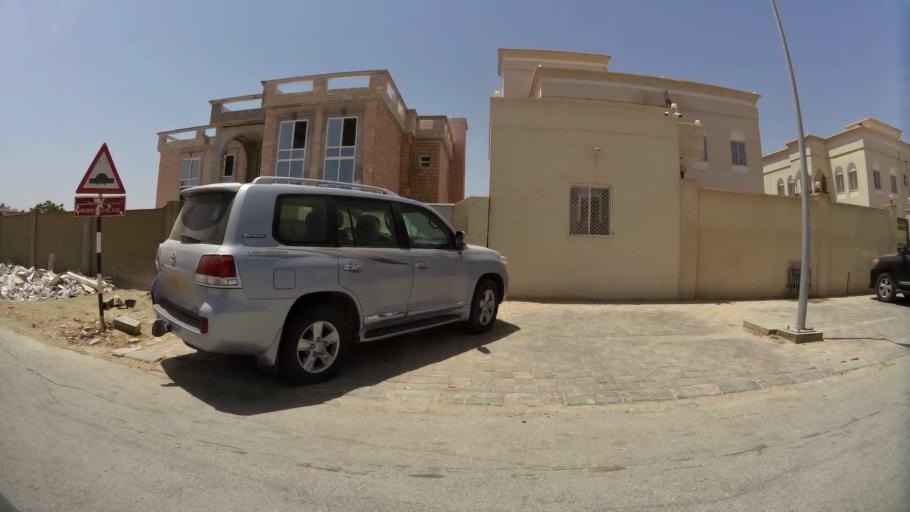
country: OM
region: Zufar
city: Salalah
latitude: 17.0598
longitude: 54.1523
